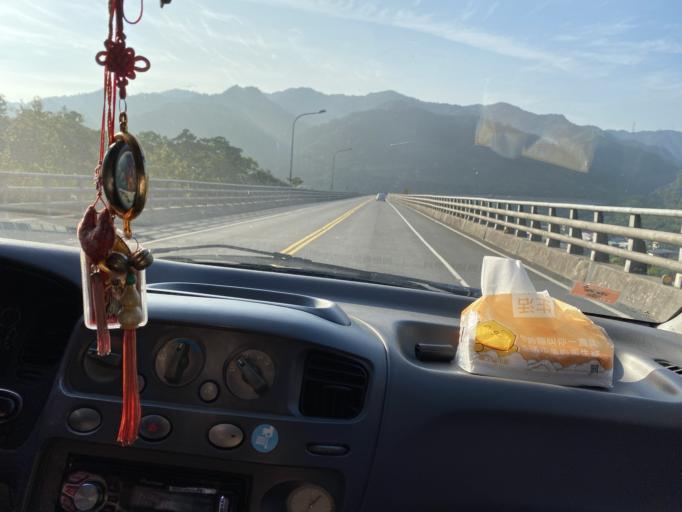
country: TW
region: Taiwan
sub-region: Keelung
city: Keelung
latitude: 25.0482
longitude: 121.7772
